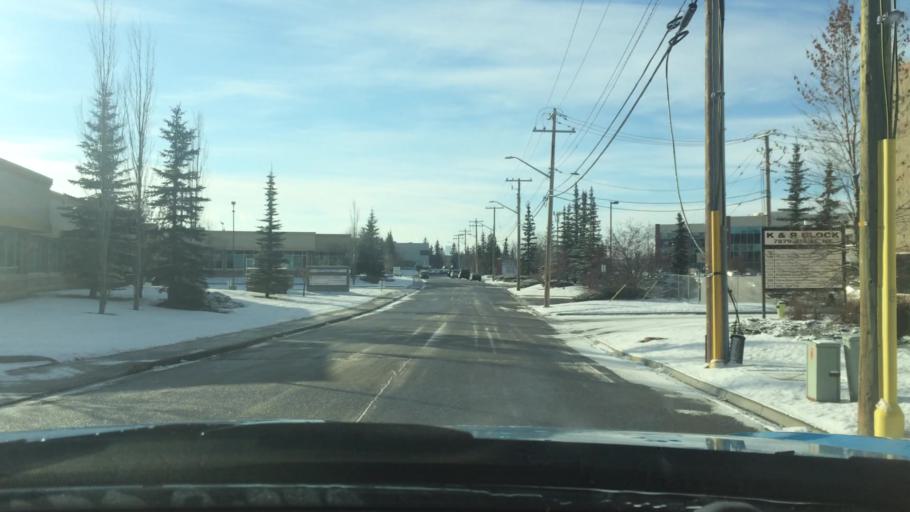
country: CA
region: Alberta
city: Calgary
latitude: 51.1211
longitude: -114.0430
